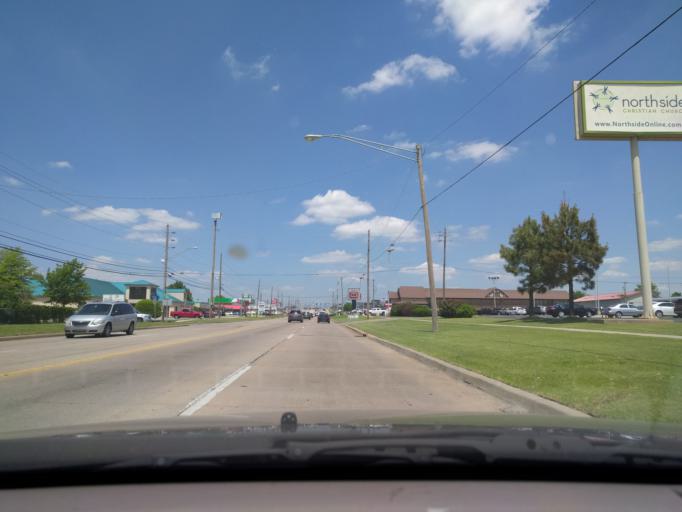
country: US
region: Oklahoma
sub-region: Tulsa County
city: Broken Arrow
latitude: 36.0658
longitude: -95.7973
